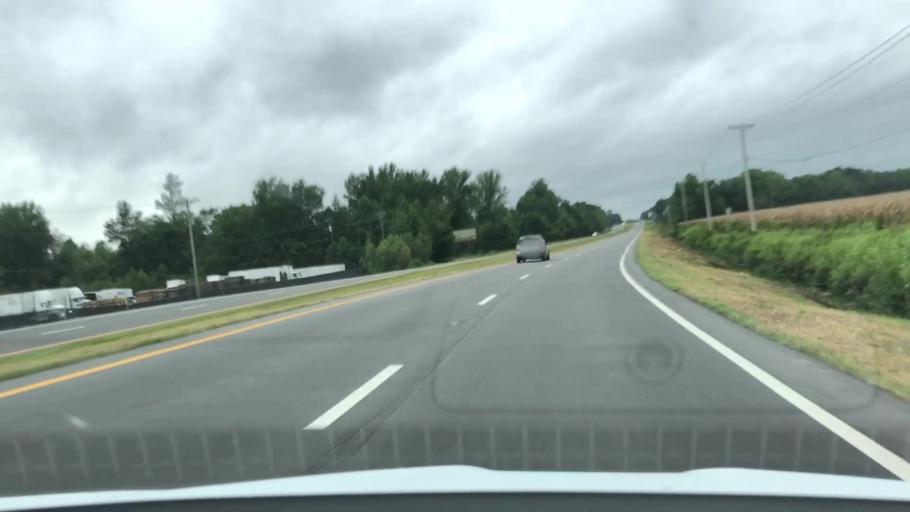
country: US
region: North Carolina
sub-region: Lenoir County
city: La Grange
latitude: 35.2705
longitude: -77.7402
